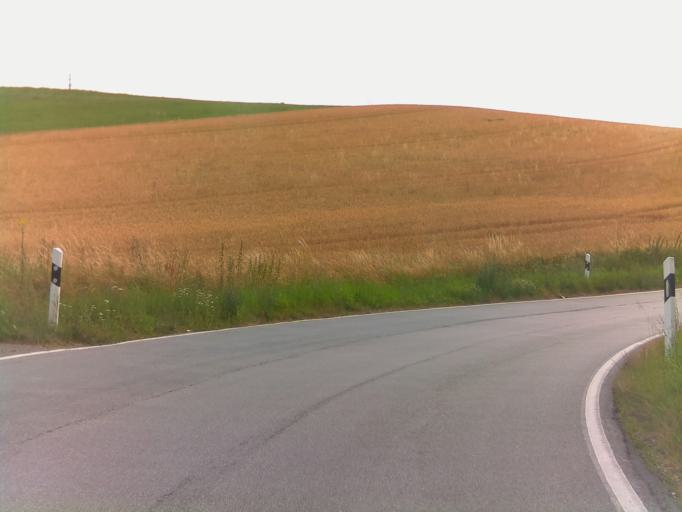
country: DE
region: Baden-Wuerttemberg
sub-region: Karlsruhe Region
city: Walldurn
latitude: 49.5139
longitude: 9.4001
